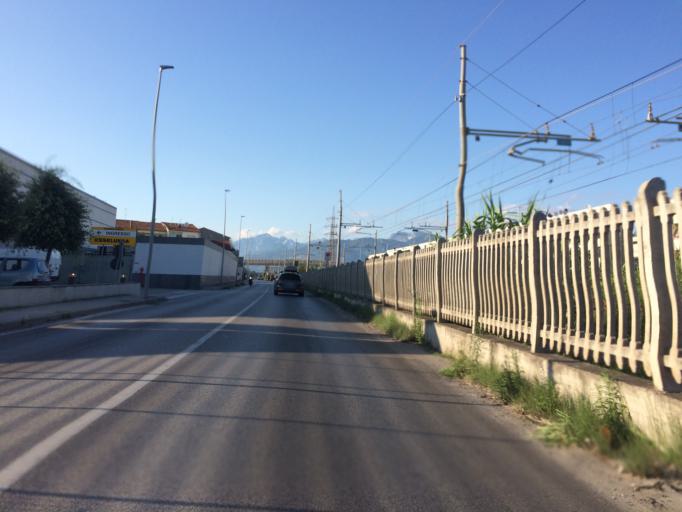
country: IT
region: Tuscany
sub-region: Provincia di Lucca
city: Viareggio
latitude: 43.8788
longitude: 10.2514
